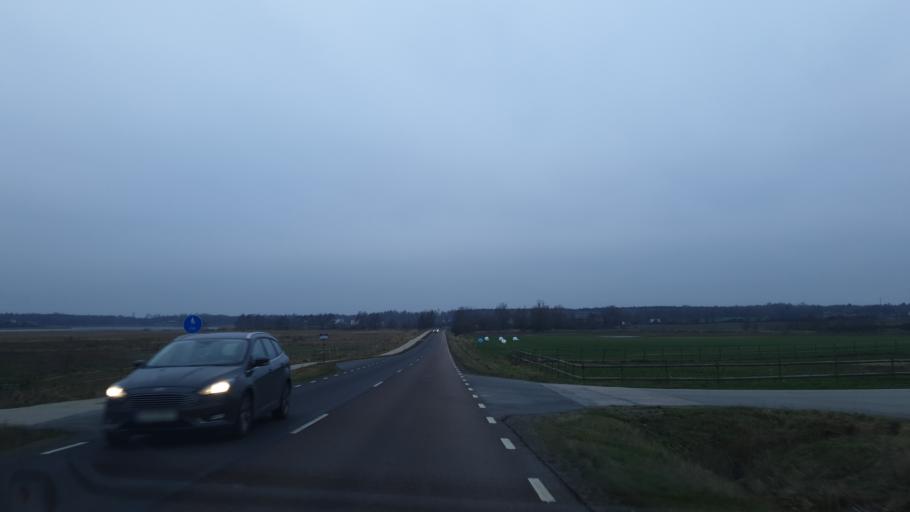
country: SE
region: Blekinge
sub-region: Karlskrona Kommun
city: Jaemjoe
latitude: 56.1719
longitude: 15.7326
